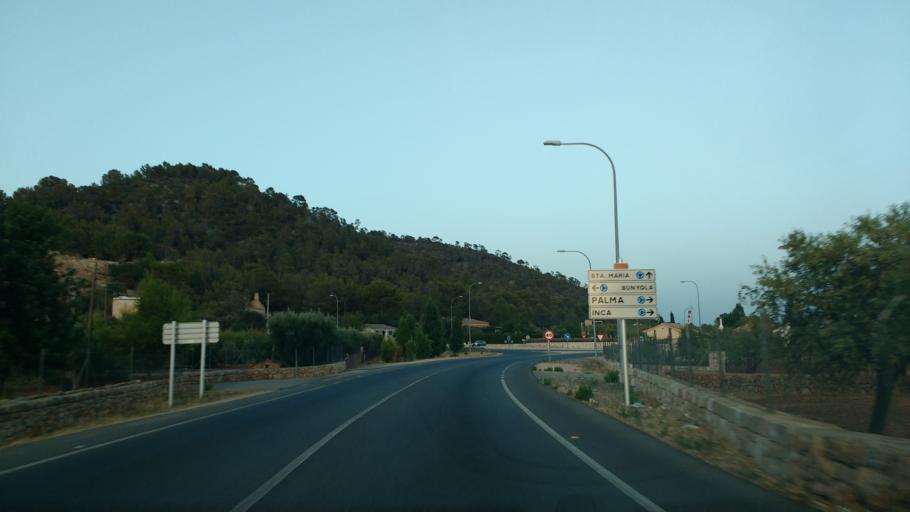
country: ES
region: Balearic Islands
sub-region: Illes Balears
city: Bunyola
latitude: 39.6668
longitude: 2.7118
